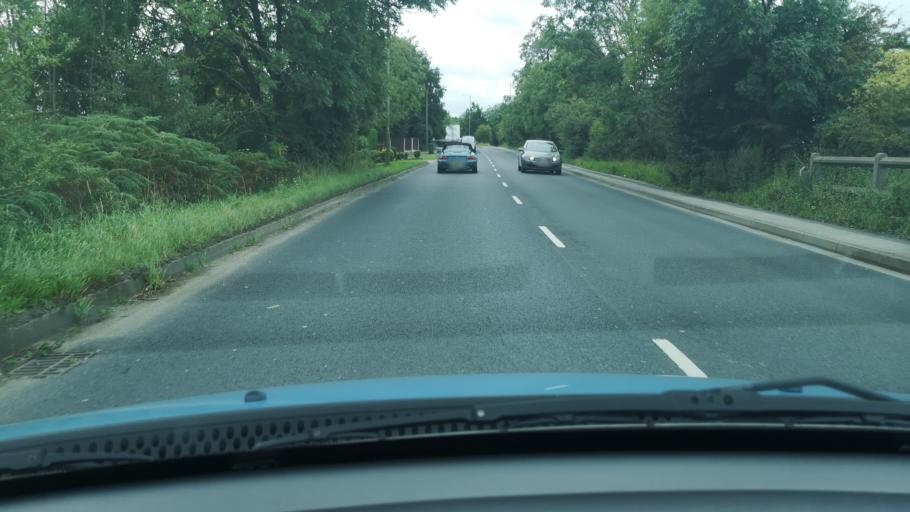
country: GB
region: England
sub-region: Barnsley
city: Shafton
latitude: 53.5934
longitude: -1.3951
